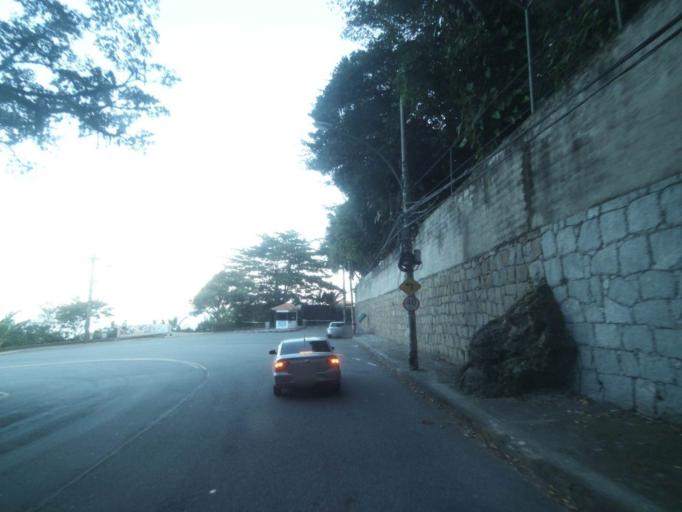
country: BR
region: Rio de Janeiro
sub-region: Rio De Janeiro
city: Rio de Janeiro
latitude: -23.0084
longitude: -43.2877
